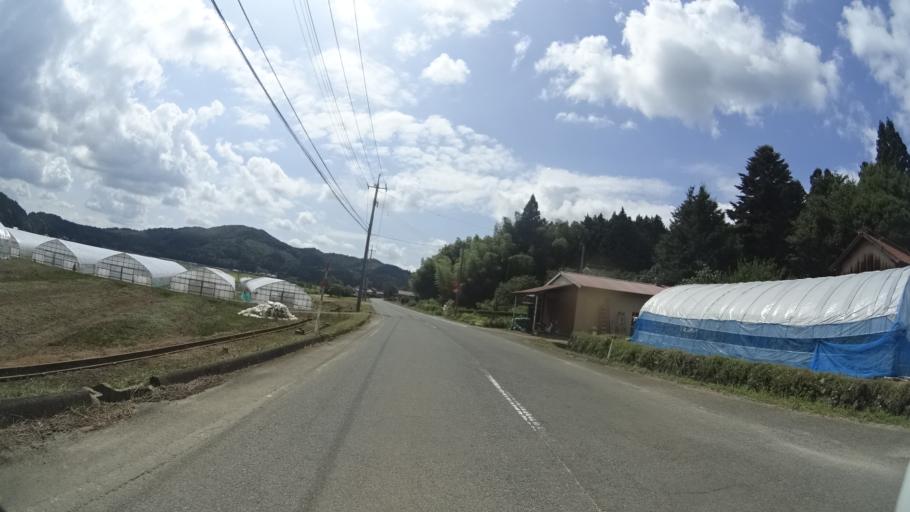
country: JP
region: Yamaguchi
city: Hagi
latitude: 34.4994
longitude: 131.5847
